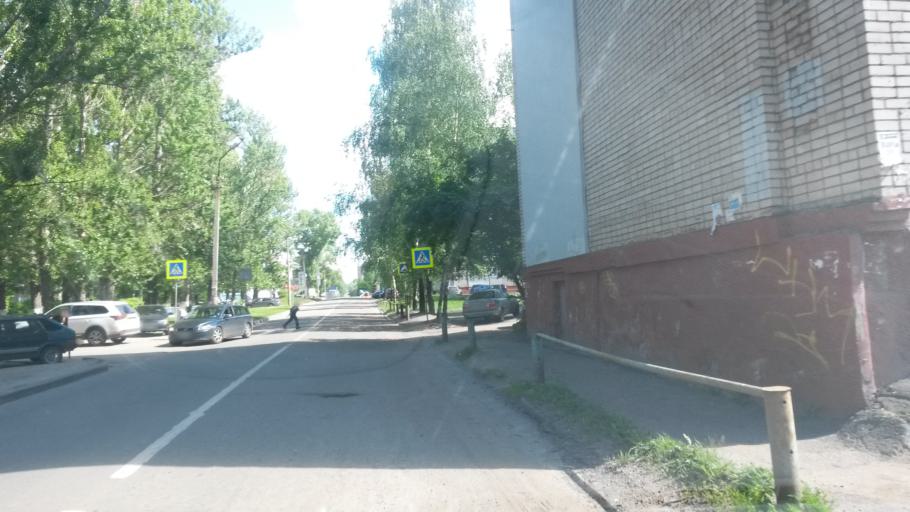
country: RU
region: Jaroslavl
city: Yaroslavl
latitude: 57.5838
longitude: 39.8268
